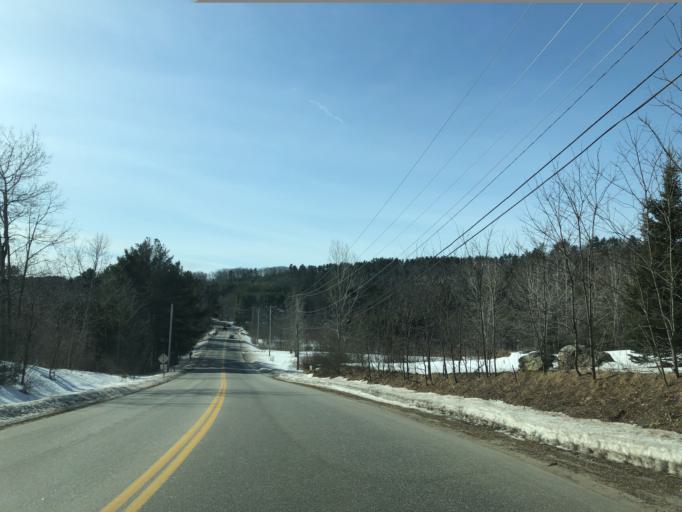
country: US
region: Maine
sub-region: Androscoggin County
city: Auburn
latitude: 44.1292
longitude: -70.2742
